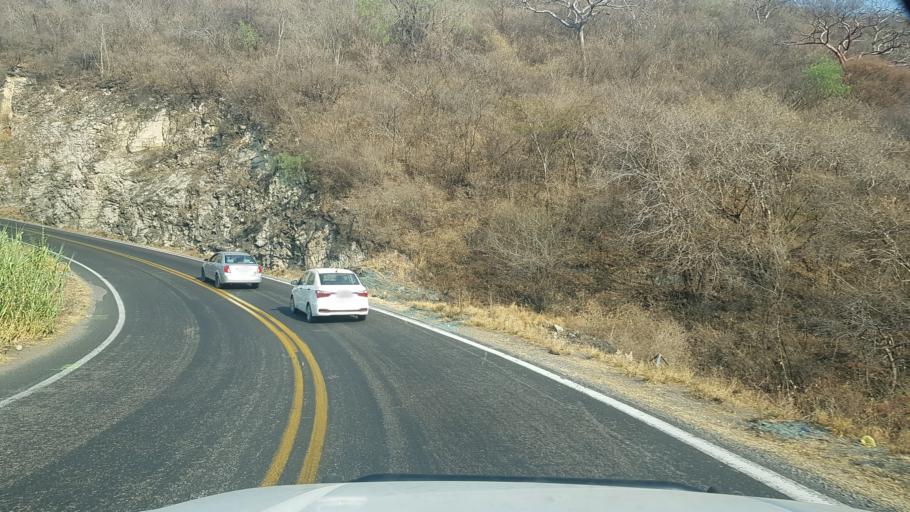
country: MX
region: Puebla
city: Calmeca
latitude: 18.6525
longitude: -98.6508
